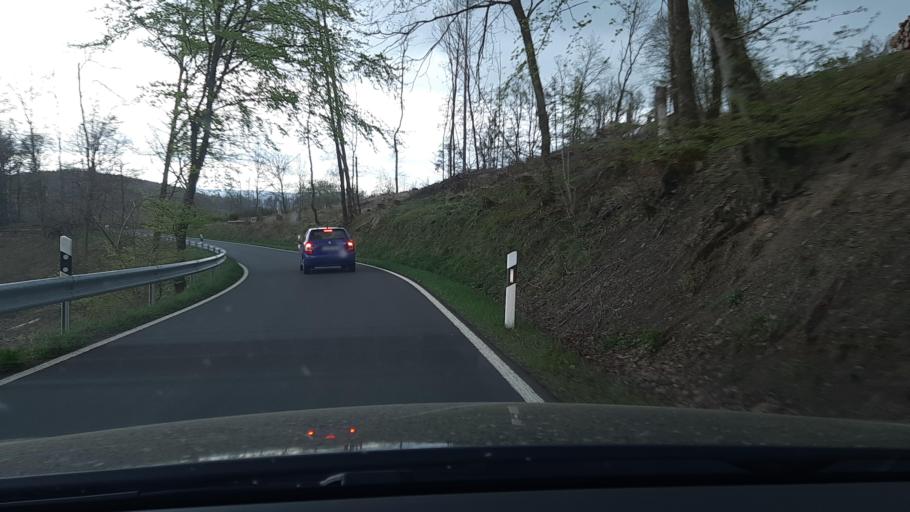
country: DE
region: North Rhine-Westphalia
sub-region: Regierungsbezirk Arnsberg
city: Bad Laasphe
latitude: 50.8877
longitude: 8.3868
